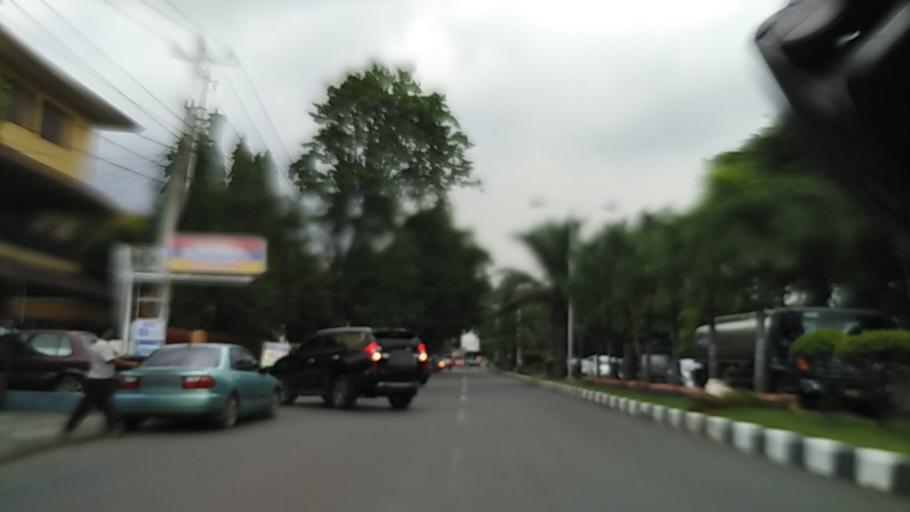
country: ID
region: Central Java
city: Semarang
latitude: -6.9855
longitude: 110.3844
